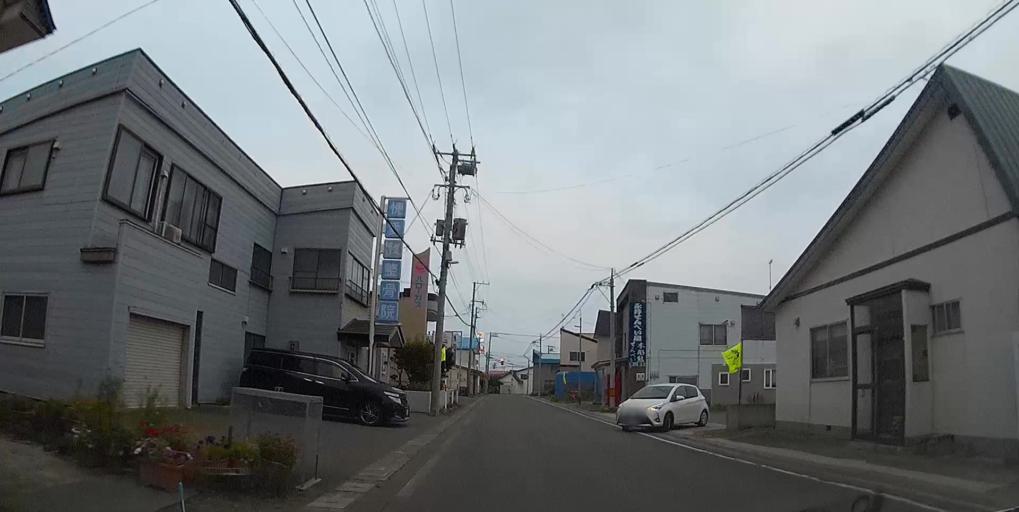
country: JP
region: Hokkaido
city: Nanae
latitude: 42.2548
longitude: 140.2647
